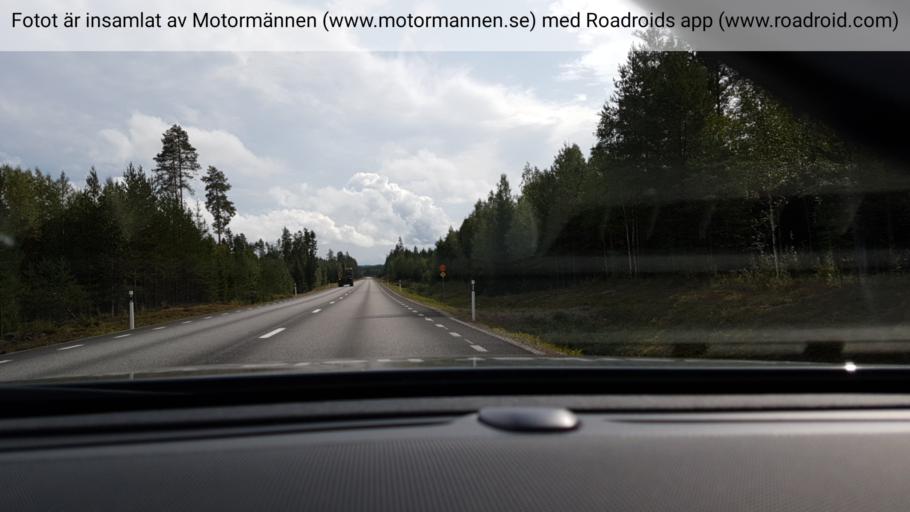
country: SE
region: Dalarna
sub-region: Rattviks Kommun
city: Raettvik
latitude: 60.8164
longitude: 15.2588
